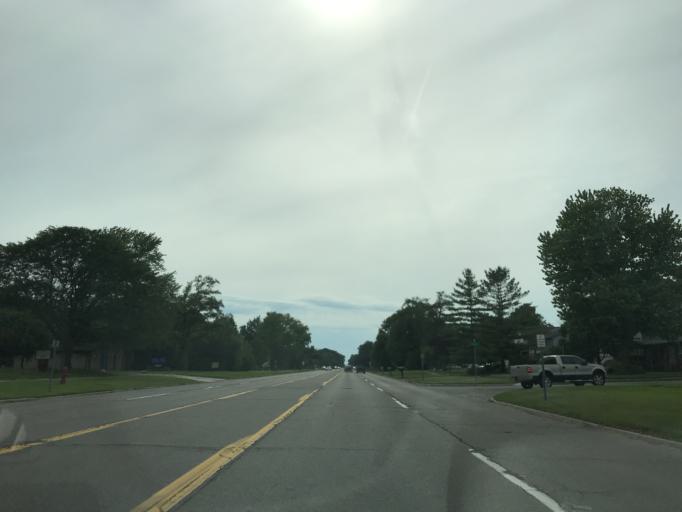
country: US
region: Michigan
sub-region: Wayne County
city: Livonia
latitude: 42.4126
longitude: -83.3393
